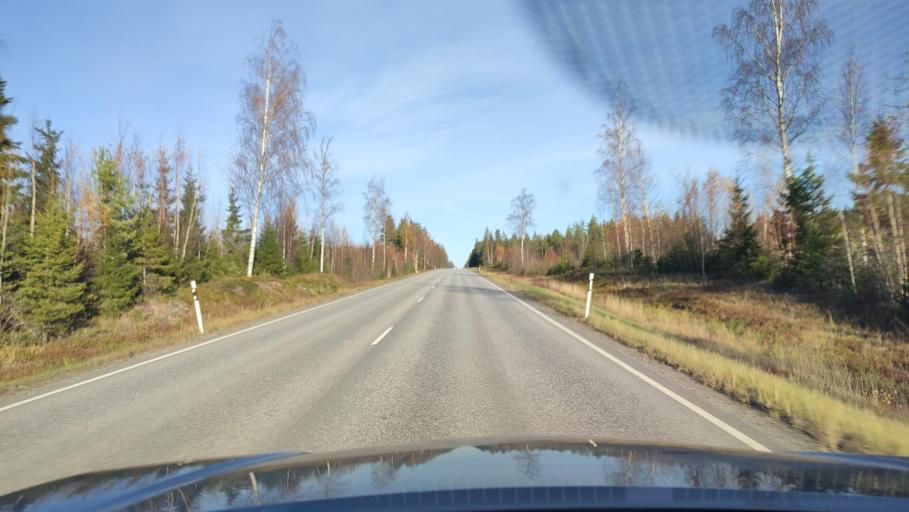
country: FI
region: Ostrobothnia
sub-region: Sydosterbotten
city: Naerpes
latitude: 62.4893
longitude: 21.4436
